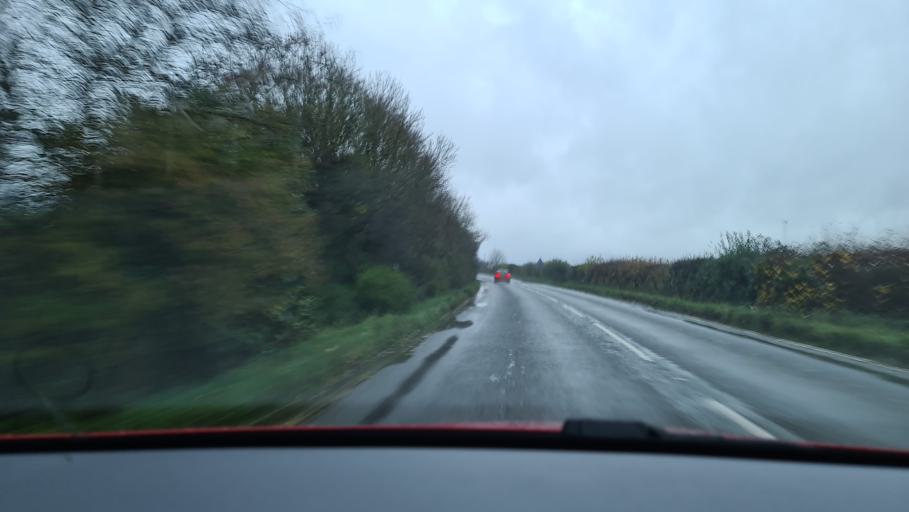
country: GB
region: England
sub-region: Oxfordshire
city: Somerton
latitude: 51.9358
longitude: -1.2151
